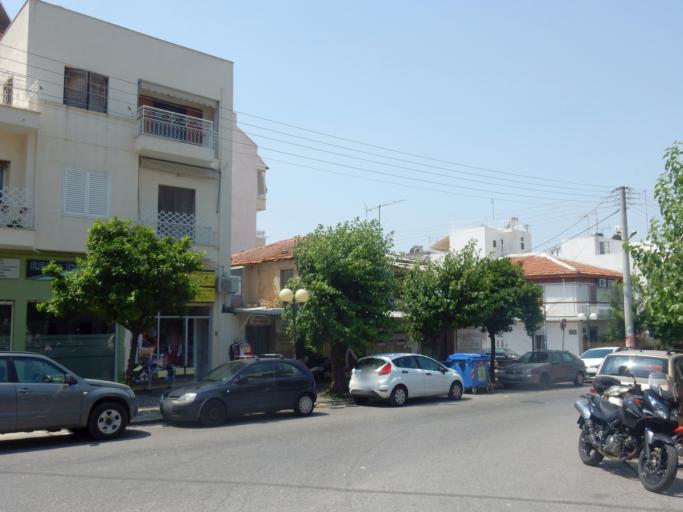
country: GR
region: Attica
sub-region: Nomarchia Athinas
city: Nea Ionia
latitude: 38.0457
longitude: 23.7535
